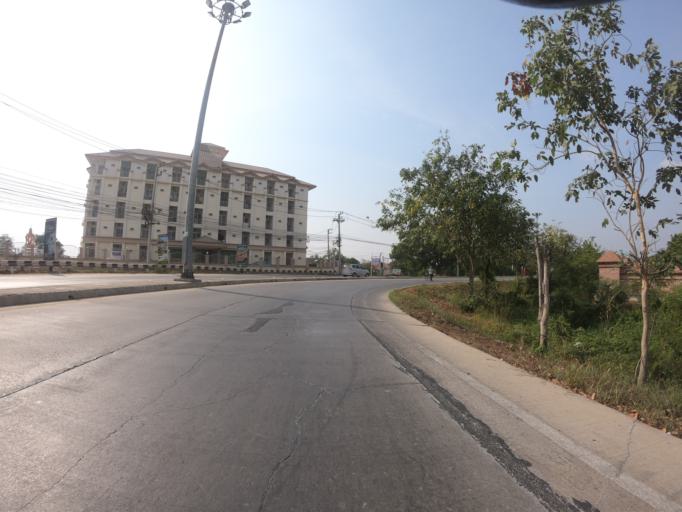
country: TH
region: Phra Nakhon Si Ayutthaya
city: Phra Nakhon Si Ayutthaya
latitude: 14.3412
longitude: 100.5924
